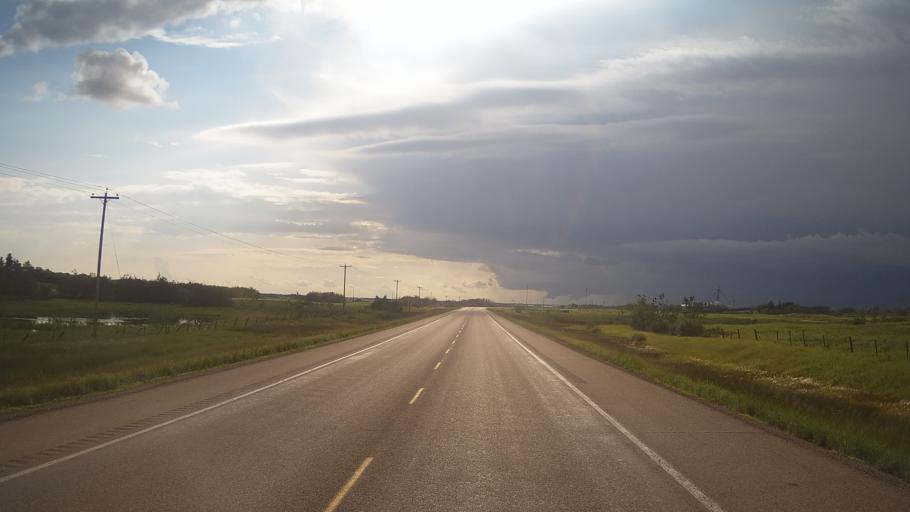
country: CA
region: Alberta
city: Vegreville
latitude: 53.2214
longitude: -112.2093
